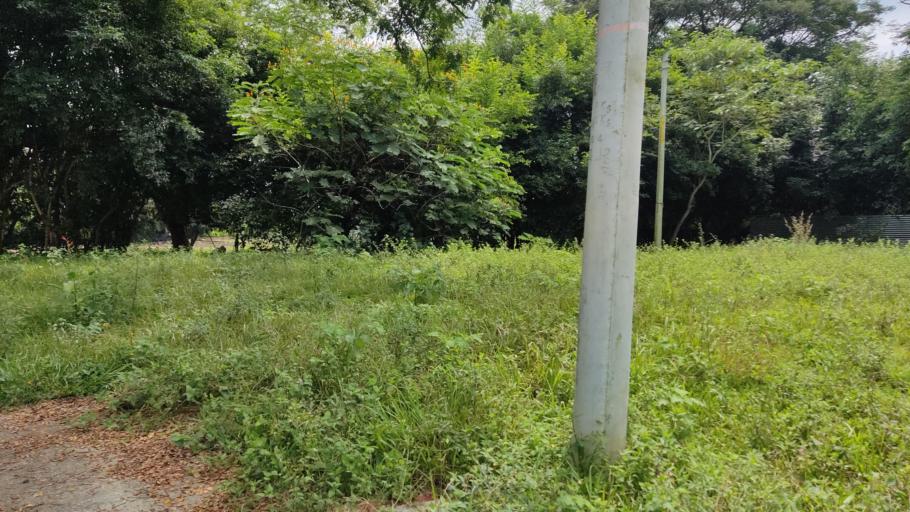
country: CO
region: Valle del Cauca
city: Jamundi
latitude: 3.3474
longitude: -76.5214
